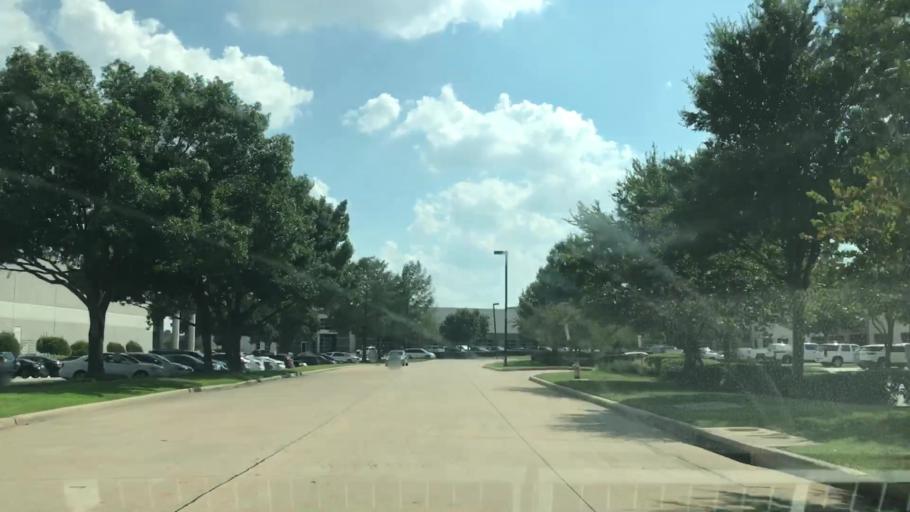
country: US
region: Texas
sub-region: Dallas County
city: Farmers Branch
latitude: 32.9428
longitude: -96.9210
